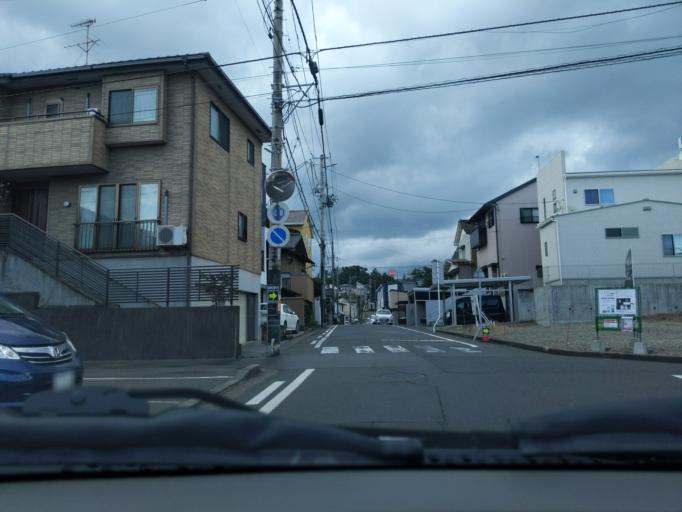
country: JP
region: Niigata
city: Niigata-shi
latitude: 37.9295
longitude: 139.0436
